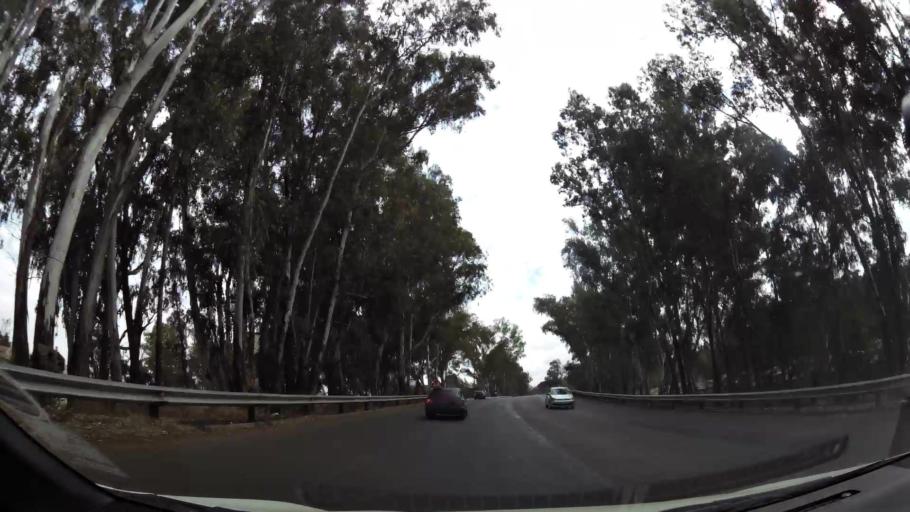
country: ZA
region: Gauteng
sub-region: Sedibeng District Municipality
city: Meyerton
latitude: -26.4179
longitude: 28.0895
